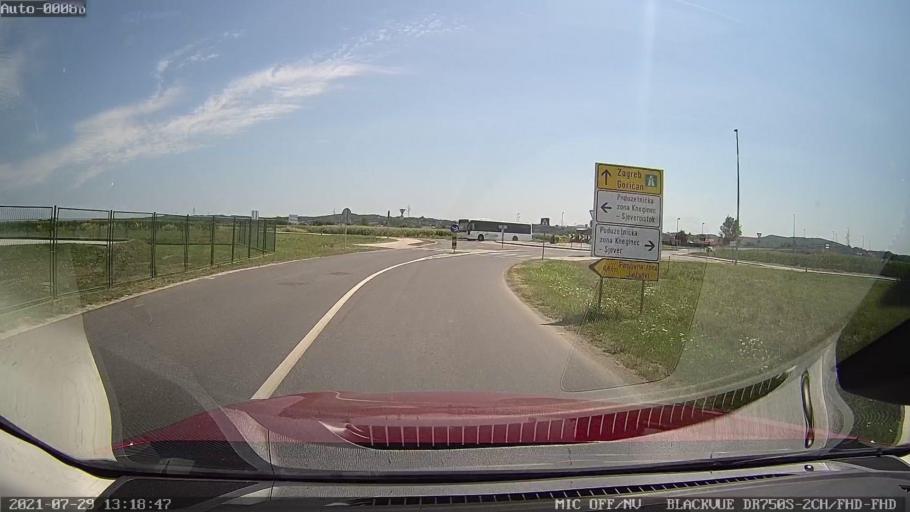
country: HR
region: Varazdinska
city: Varazdin
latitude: 46.2675
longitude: 16.3813
